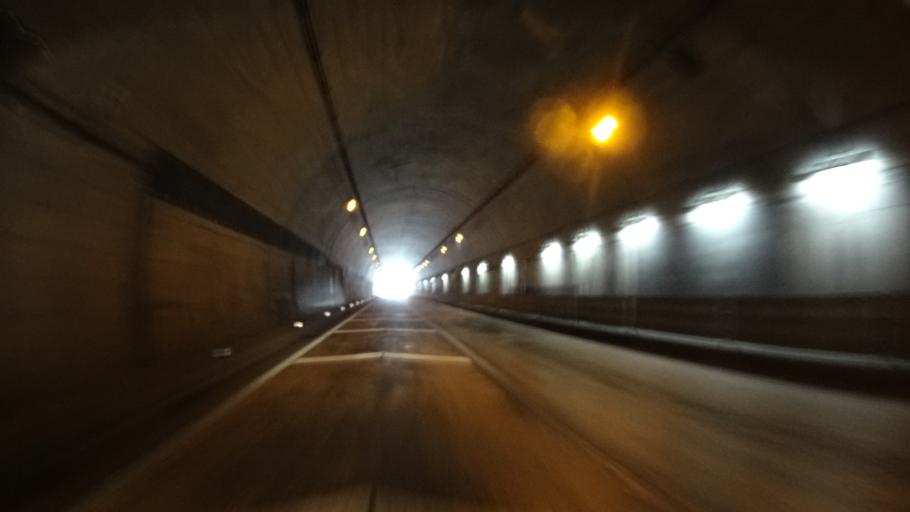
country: JP
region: Niigata
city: Muikamachi
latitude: 37.1349
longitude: 138.9538
